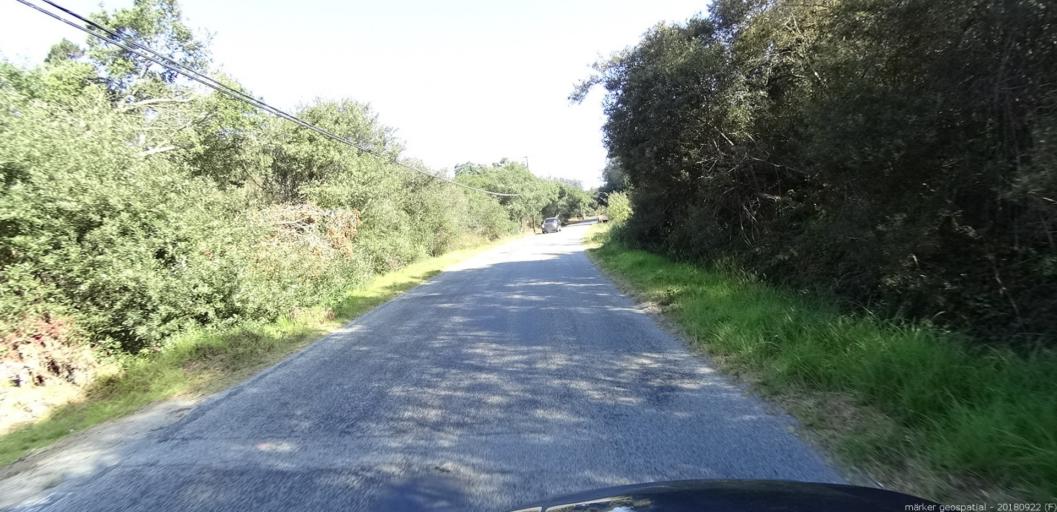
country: US
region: California
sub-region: Monterey County
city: Prunedale
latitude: 36.8135
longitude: -121.6504
